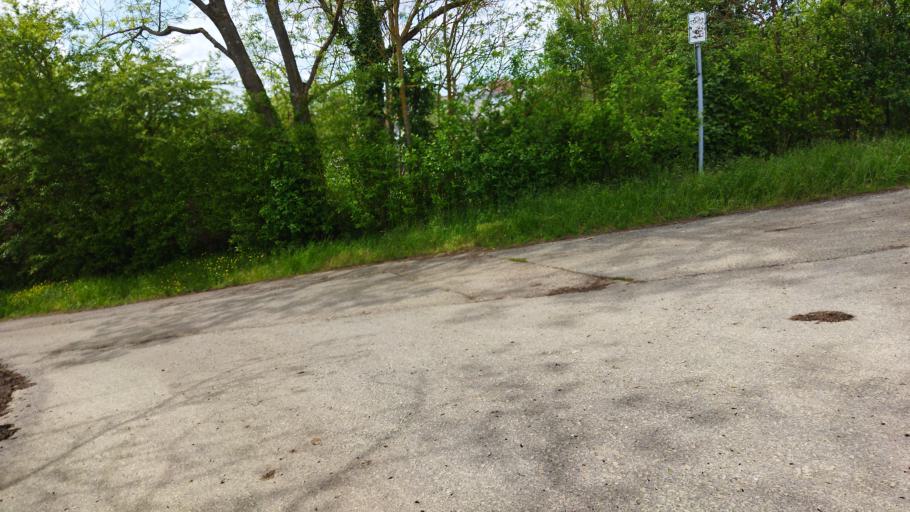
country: DE
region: Baden-Wuerttemberg
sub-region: Regierungsbezirk Stuttgart
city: Bad Rappenau
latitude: 49.2111
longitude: 9.1016
